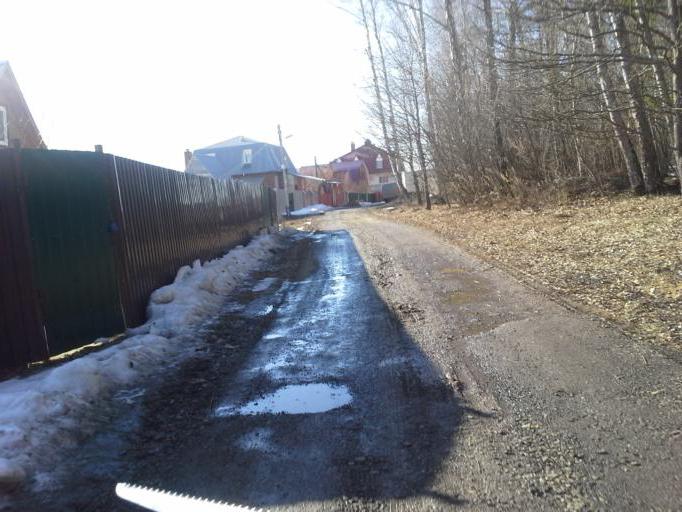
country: RU
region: Moskovskaya
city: Filimonki
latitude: 55.5473
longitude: 37.3865
